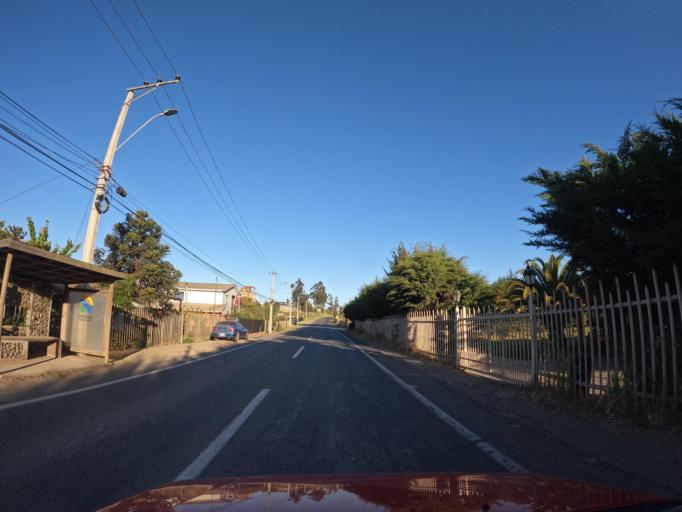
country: CL
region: Maule
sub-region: Provincia de Talca
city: Talca
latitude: -34.9954
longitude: -71.9714
